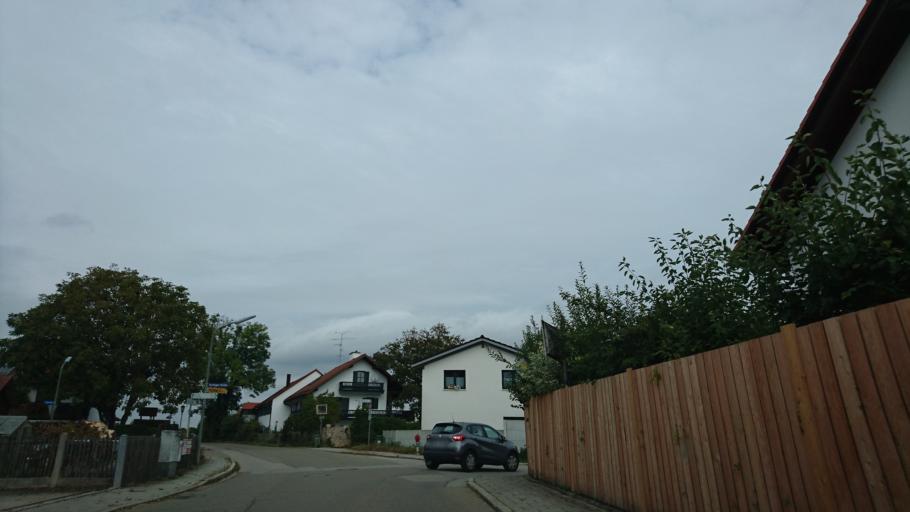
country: DE
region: Bavaria
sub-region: Upper Bavaria
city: Vaterstetten
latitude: 48.1156
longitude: 11.7967
